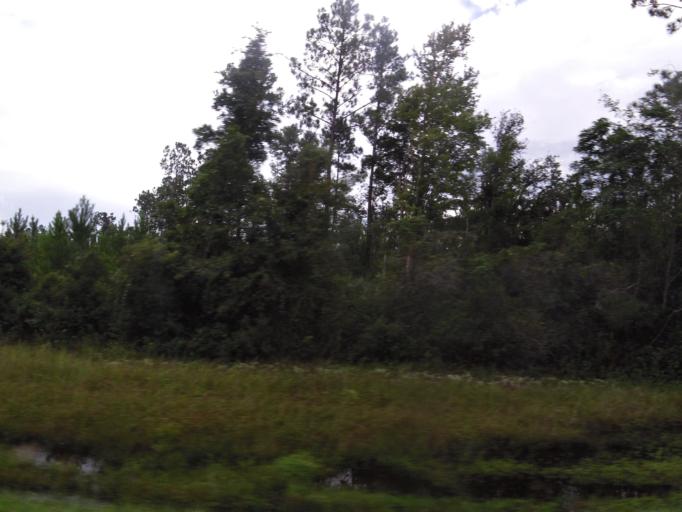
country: US
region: Florida
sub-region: Duval County
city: Baldwin
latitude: 30.4017
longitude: -81.9766
